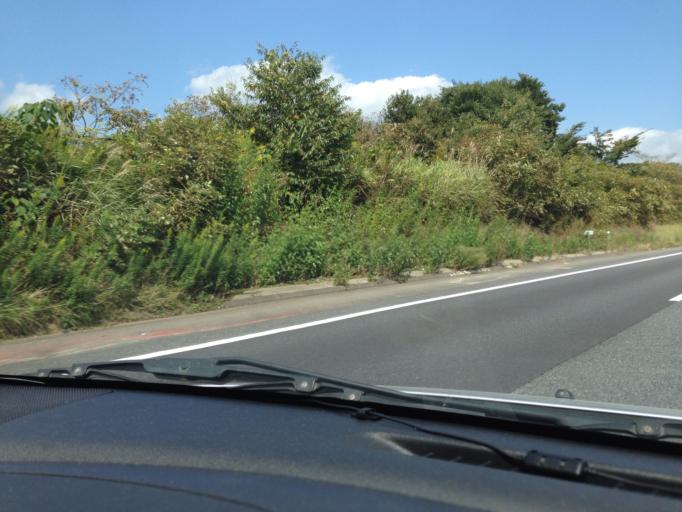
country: JP
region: Ibaraki
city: Ishioka
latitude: 36.1397
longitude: 140.2049
